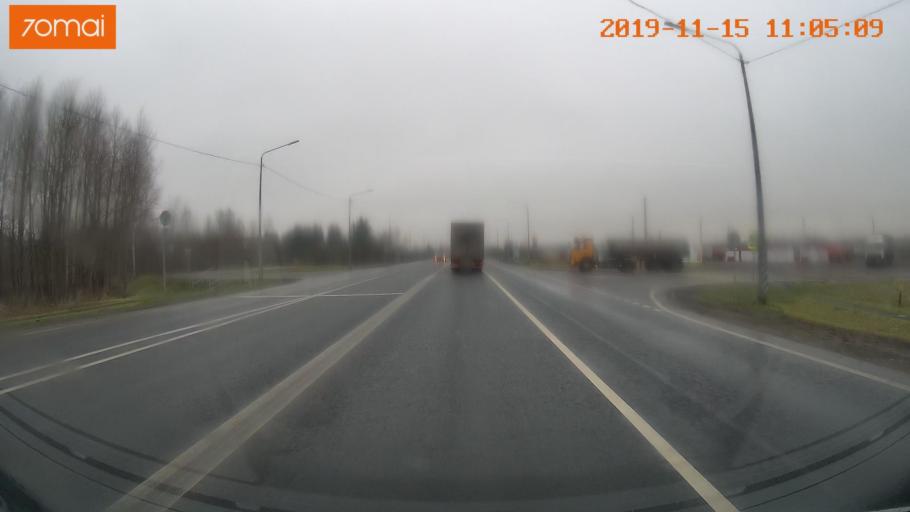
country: RU
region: Vologda
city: Chebsara
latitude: 59.1184
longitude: 38.9989
